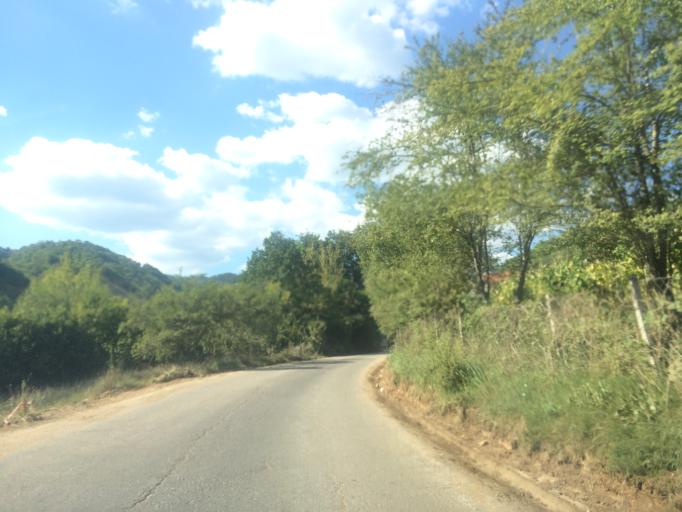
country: MK
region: Makedonska Kamenica
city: Makedonska Kamenica
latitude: 42.0408
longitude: 22.5778
